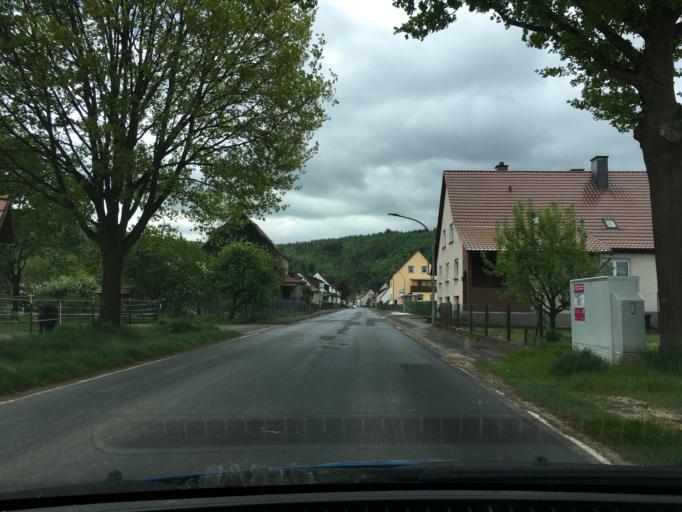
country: DE
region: Lower Saxony
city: Bodenfelde
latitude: 51.6327
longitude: 9.5227
